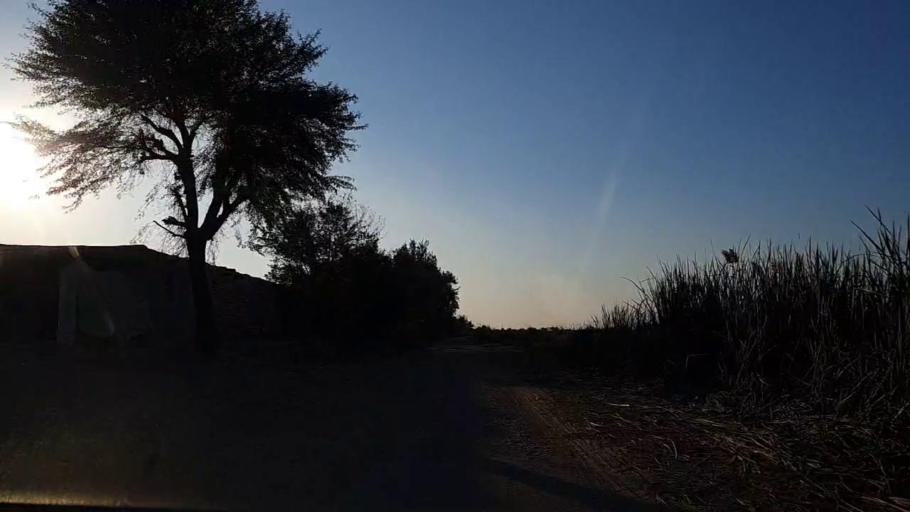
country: PK
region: Sindh
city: Khadro
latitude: 26.2791
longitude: 68.8252
